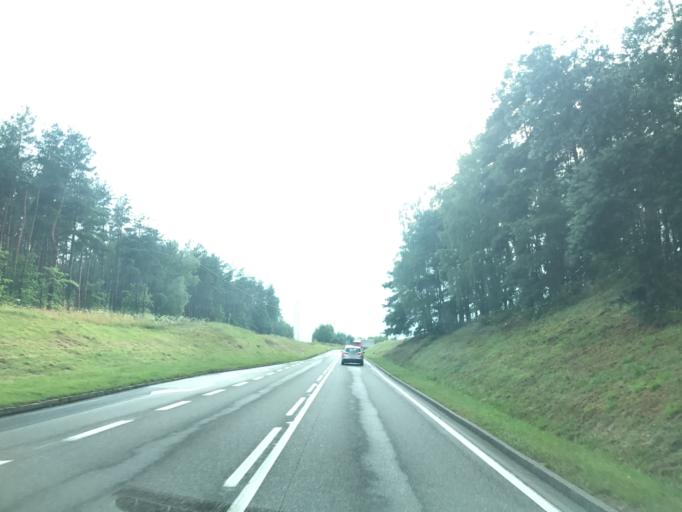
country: PL
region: Pomeranian Voivodeship
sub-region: Powiat czluchowski
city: Przechlewo
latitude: 53.7321
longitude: 17.2107
